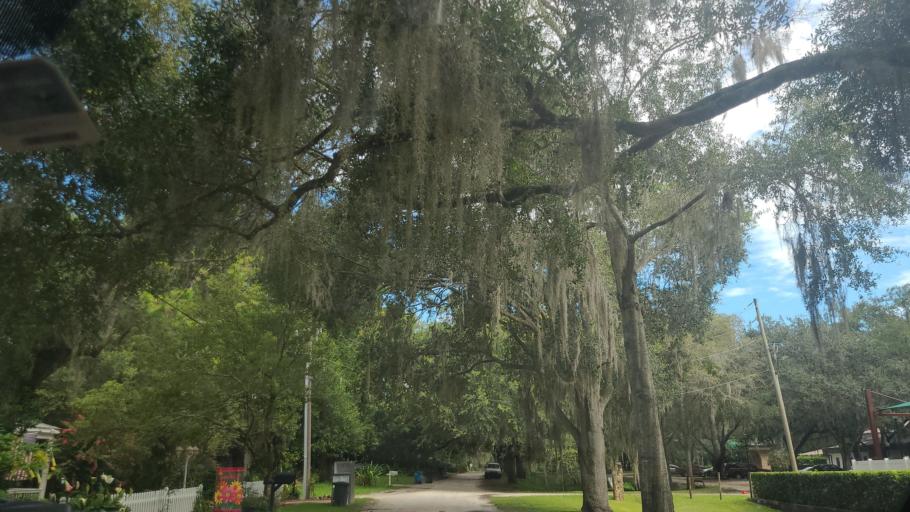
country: US
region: Florida
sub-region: Orange County
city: Windermere
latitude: 28.4961
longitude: -81.5366
